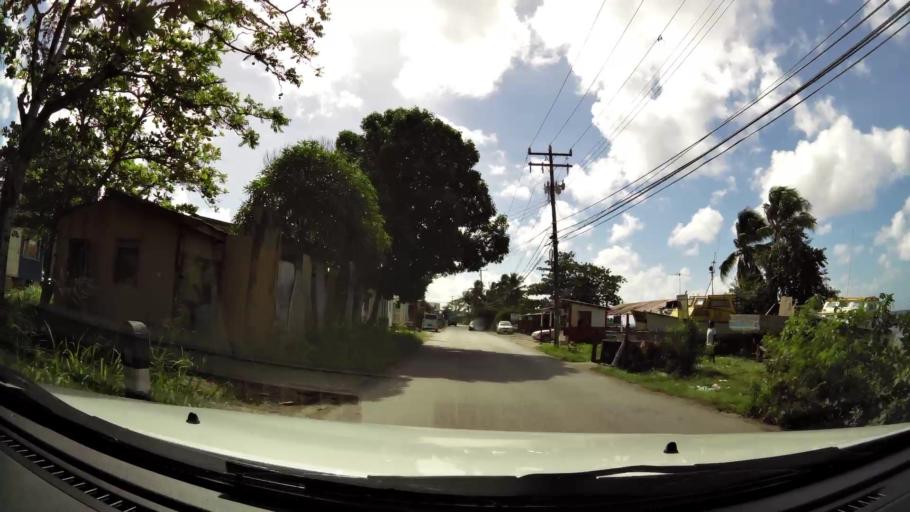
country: BB
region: Saint Lucy
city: Checker Hall
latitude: 13.2685
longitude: -59.6449
